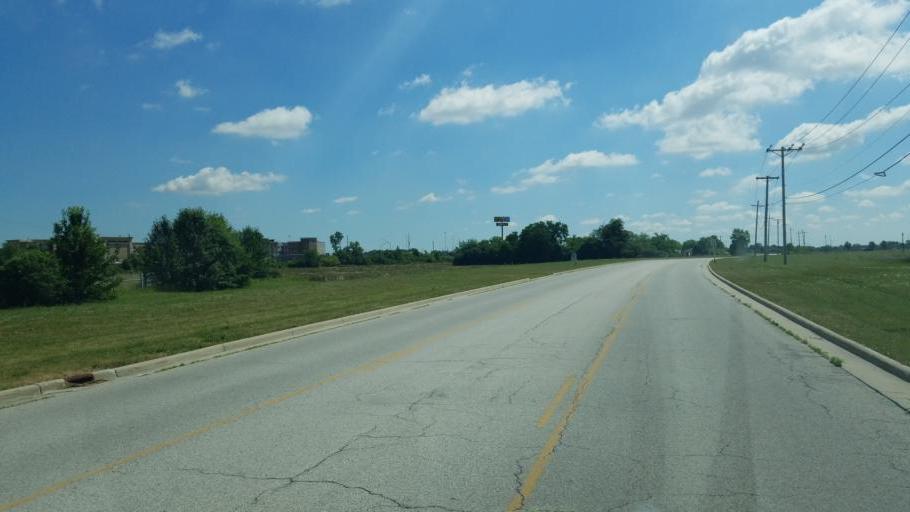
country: US
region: Ohio
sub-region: Wood County
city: Perrysburg
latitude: 41.5629
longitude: -83.5845
